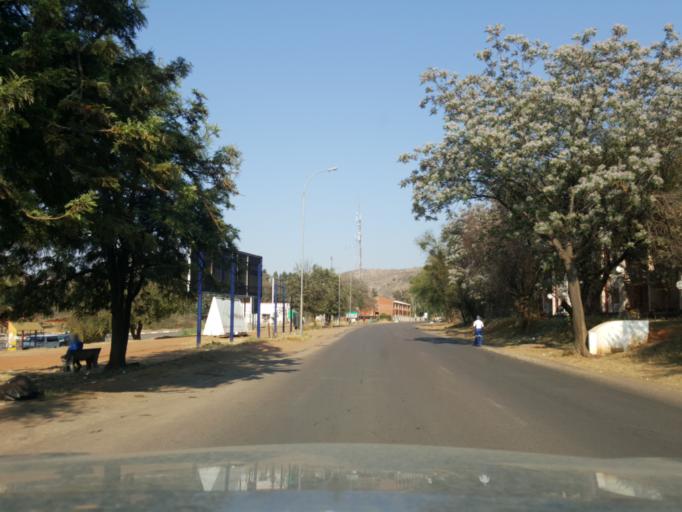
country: BW
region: South East
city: Lobatse
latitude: -25.2283
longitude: 25.6731
